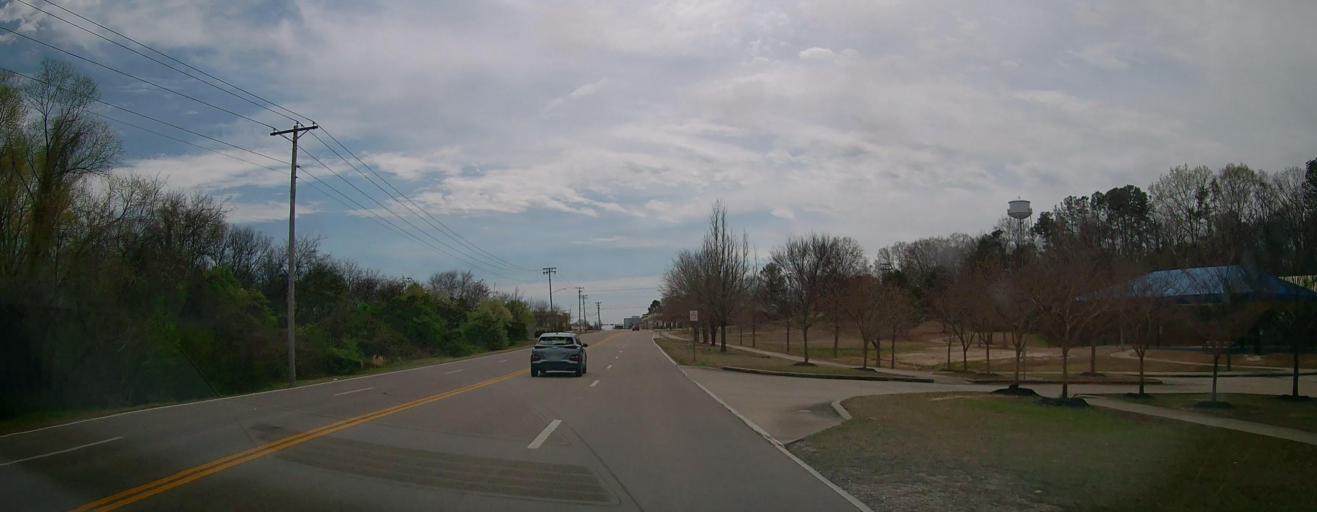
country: US
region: Mississippi
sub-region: Lee County
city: Tupelo
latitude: 34.2666
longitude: -88.7035
